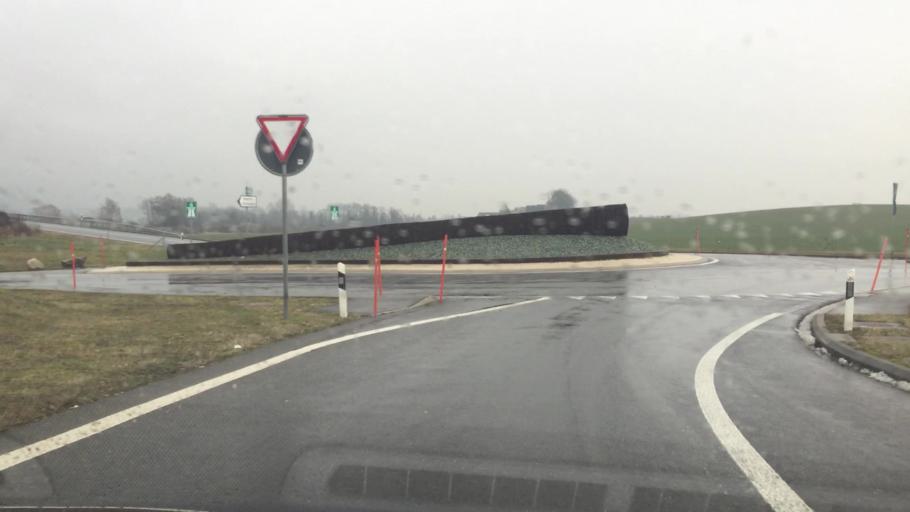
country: CH
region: Vaud
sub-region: Jura-Nord vaudois District
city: Grandson
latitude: 46.8222
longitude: 6.6595
